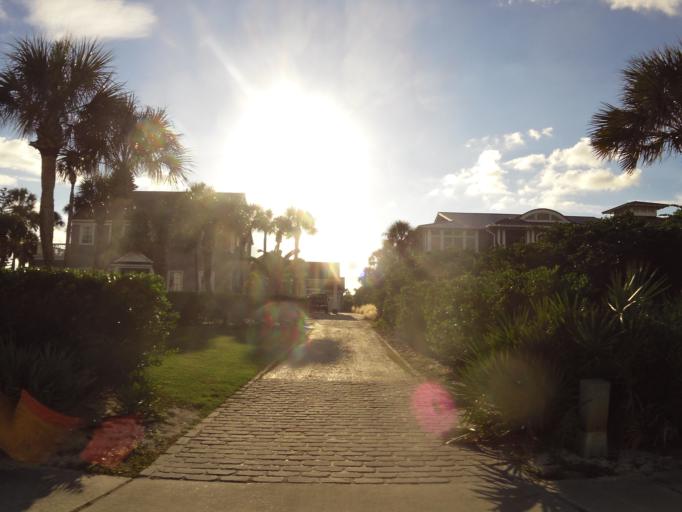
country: US
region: Florida
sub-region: Saint Johns County
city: Ponte Vedra Beach
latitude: 30.2314
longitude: -81.3757
